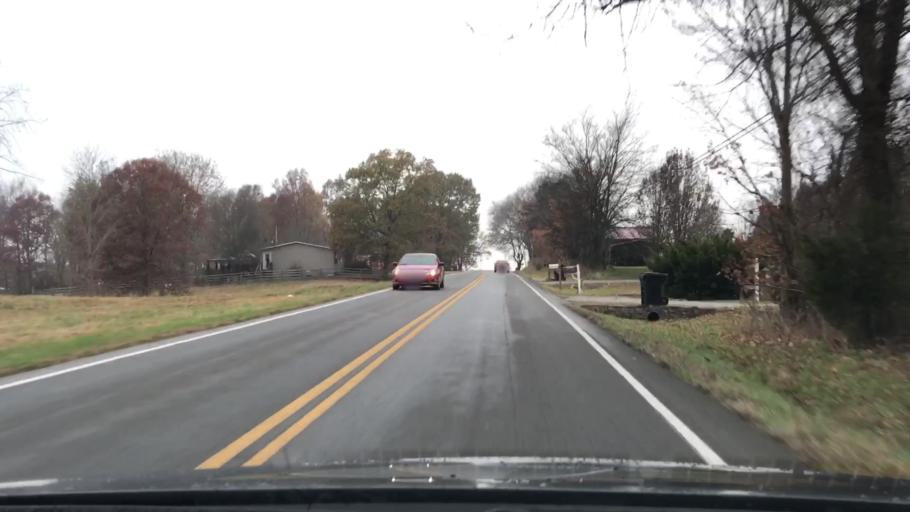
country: US
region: Tennessee
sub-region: Sumner County
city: Portland
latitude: 36.6960
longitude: -86.3893
